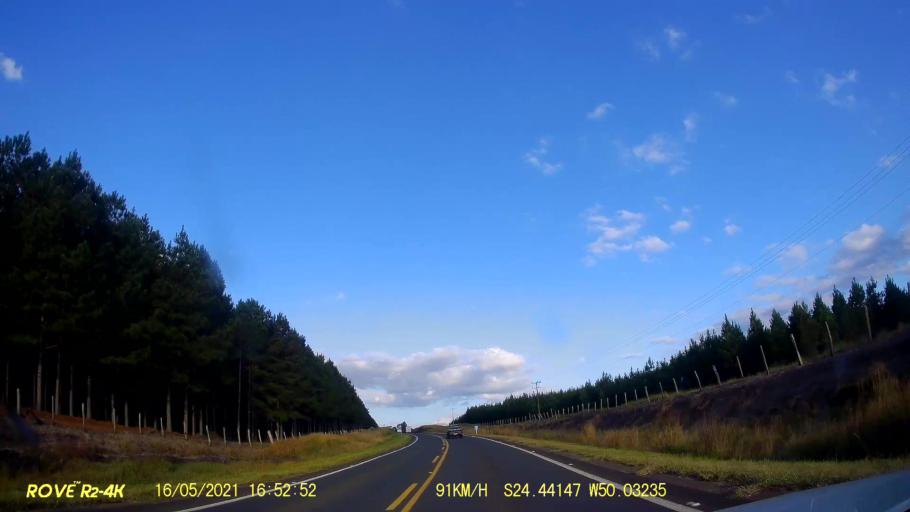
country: BR
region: Parana
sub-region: Pirai Do Sul
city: Pirai do Sul
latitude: -24.4414
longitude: -50.0323
